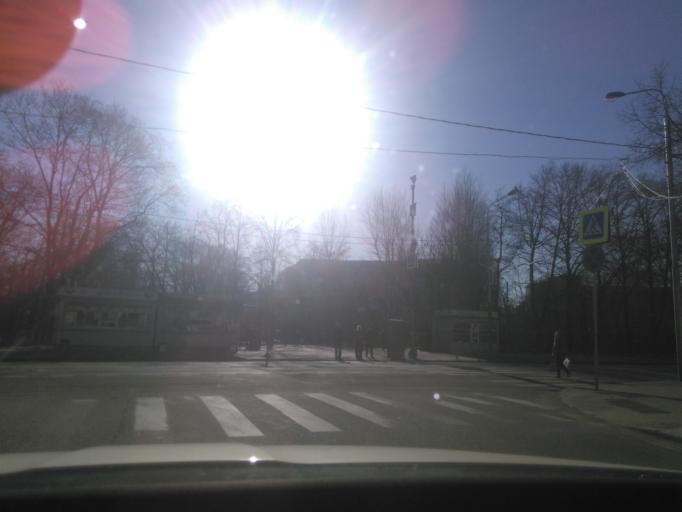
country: RU
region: Moskovskaya
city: Dorogomilovo
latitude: 55.7353
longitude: 37.5741
